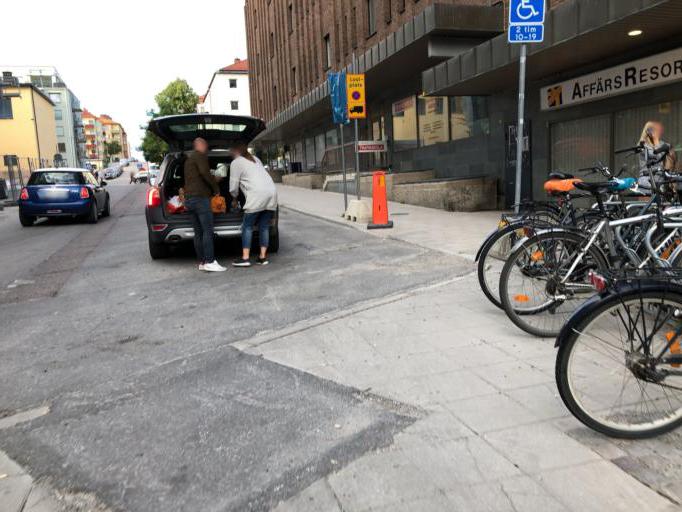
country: SE
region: Stockholm
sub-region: Sundbybergs Kommun
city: Sundbyberg
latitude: 59.3612
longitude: 17.9722
